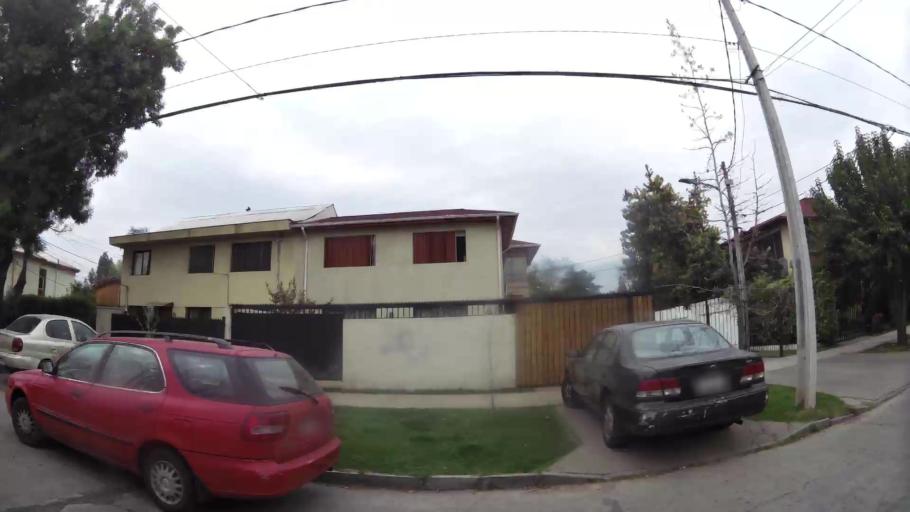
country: CL
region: Santiago Metropolitan
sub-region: Provincia de Santiago
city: Villa Presidente Frei, Nunoa, Santiago, Chile
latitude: -33.4620
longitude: -70.5895
